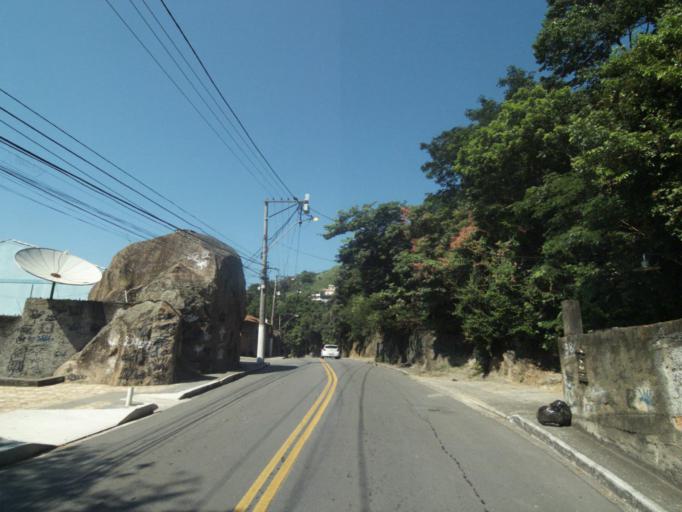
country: BR
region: Rio de Janeiro
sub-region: Niteroi
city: Niteroi
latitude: -22.9283
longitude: -43.1179
